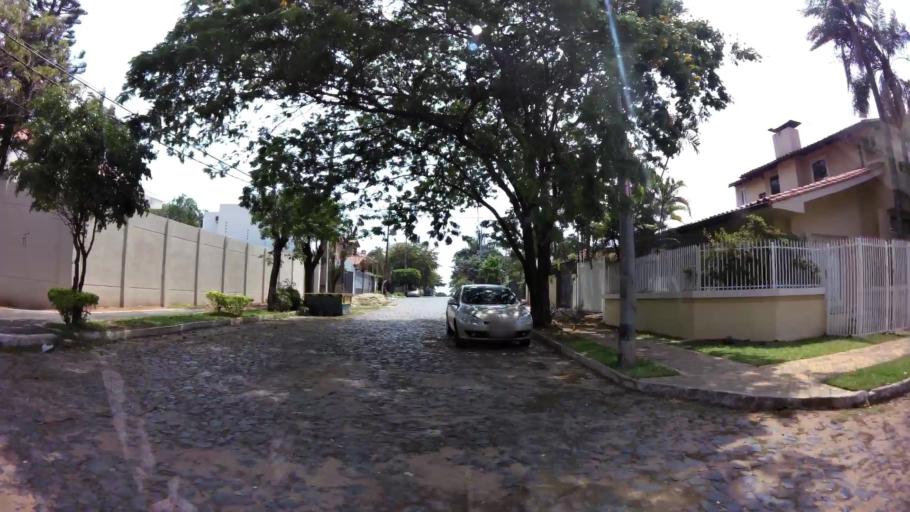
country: PY
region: Asuncion
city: Asuncion
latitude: -25.2796
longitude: -57.5959
